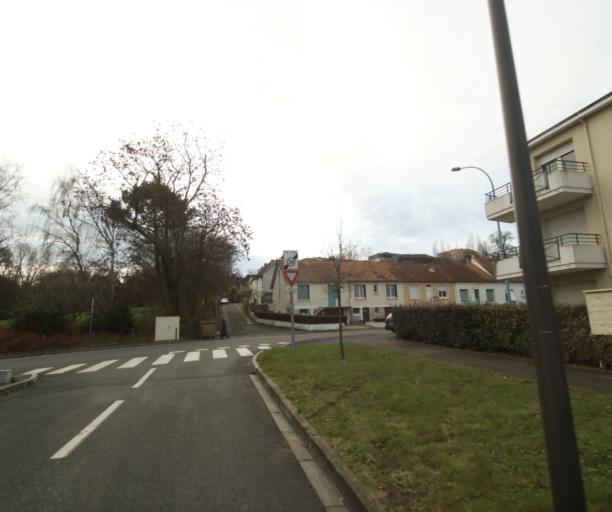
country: FR
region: Pays de la Loire
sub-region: Departement de la Sarthe
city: Coulaines
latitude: 48.0173
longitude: 0.2057
